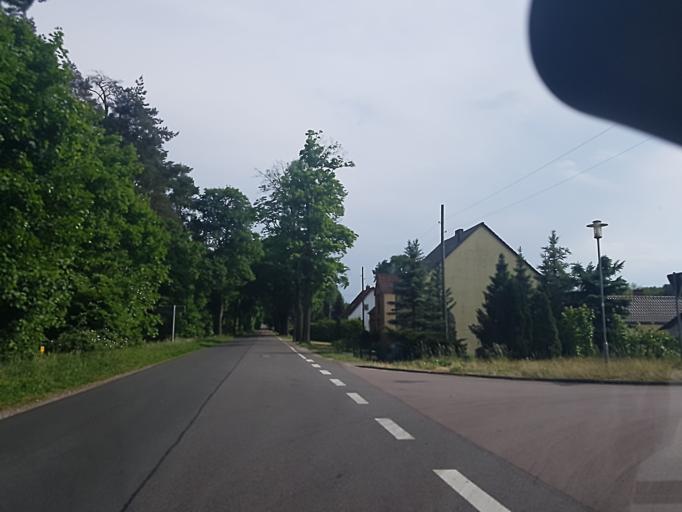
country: DE
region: Saxony-Anhalt
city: Nudersdorf
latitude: 51.9366
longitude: 12.6012
